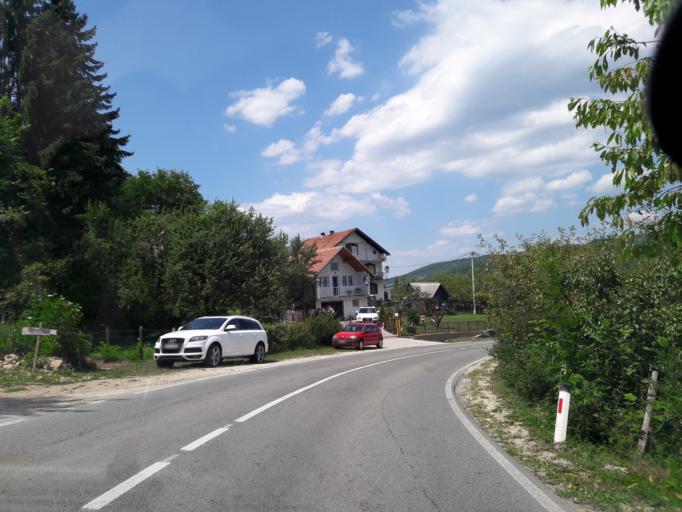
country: BA
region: Republika Srpska
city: Sipovo
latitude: 44.2027
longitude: 17.1434
